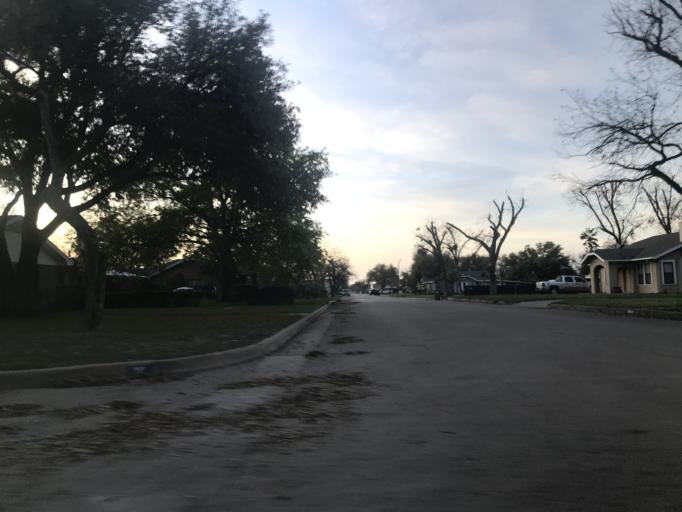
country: US
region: Texas
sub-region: Tom Green County
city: San Angelo
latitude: 31.4529
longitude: -100.4545
